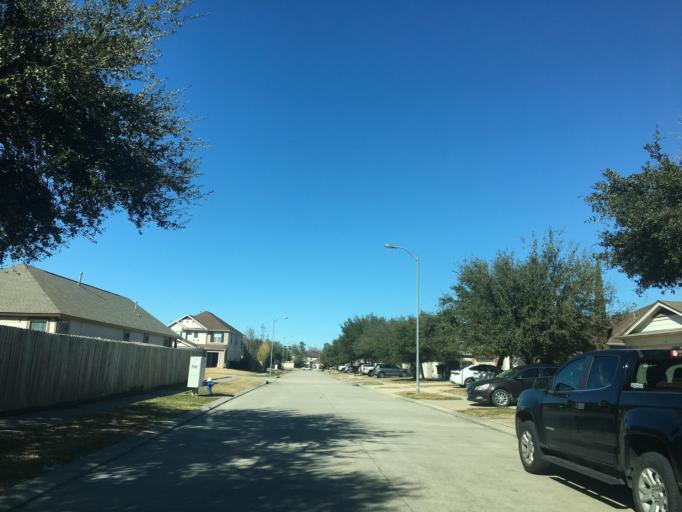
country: US
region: Texas
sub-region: Harris County
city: Spring
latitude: 30.0838
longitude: -95.4621
